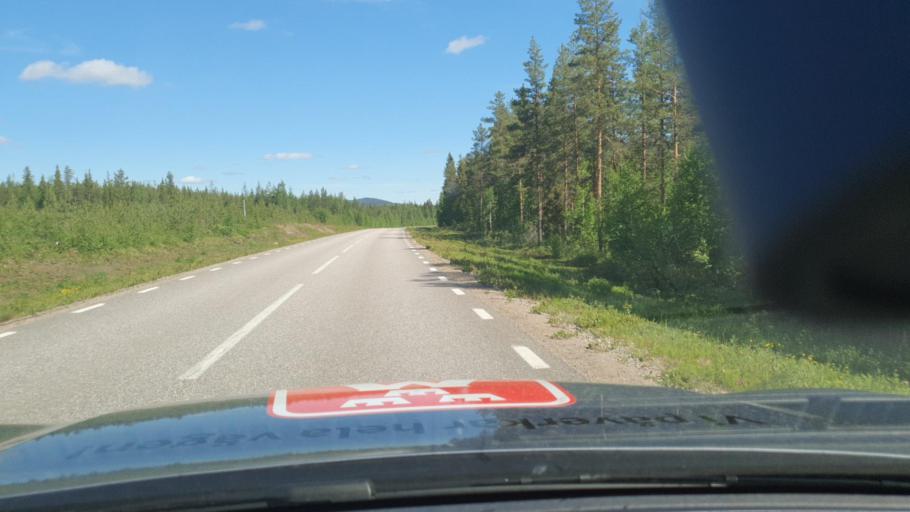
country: SE
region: Norrbotten
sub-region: Overkalix Kommun
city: OEverkalix
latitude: 66.7525
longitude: 22.6726
